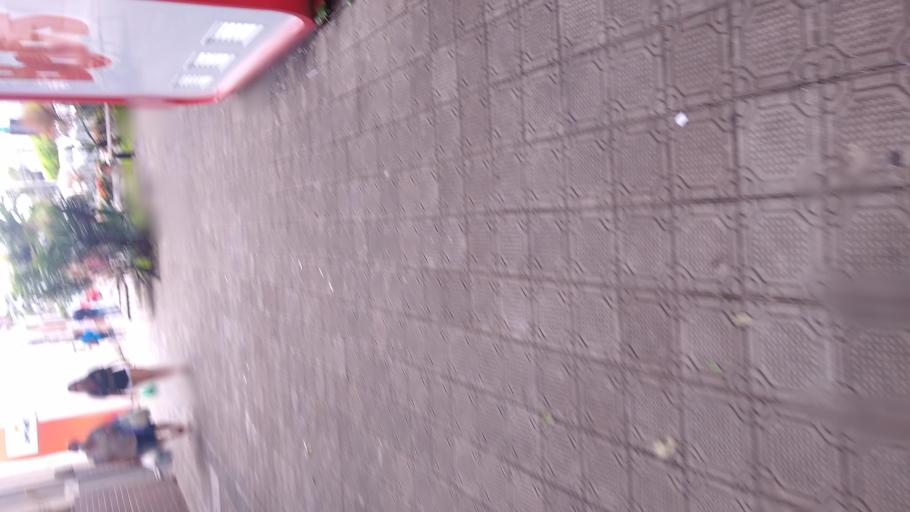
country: BR
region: Ceara
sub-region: Crato
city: Crato
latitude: -7.2343
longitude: -39.4129
